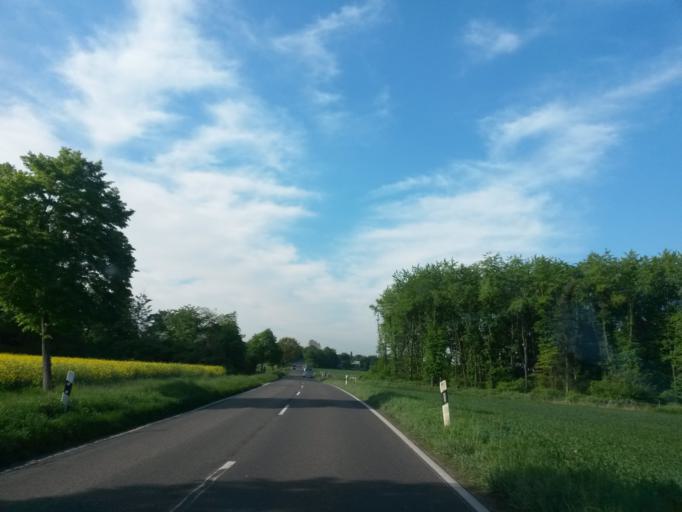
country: DE
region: North Rhine-Westphalia
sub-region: Regierungsbezirk Koln
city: Troisdorf
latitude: 50.7698
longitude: 7.1310
